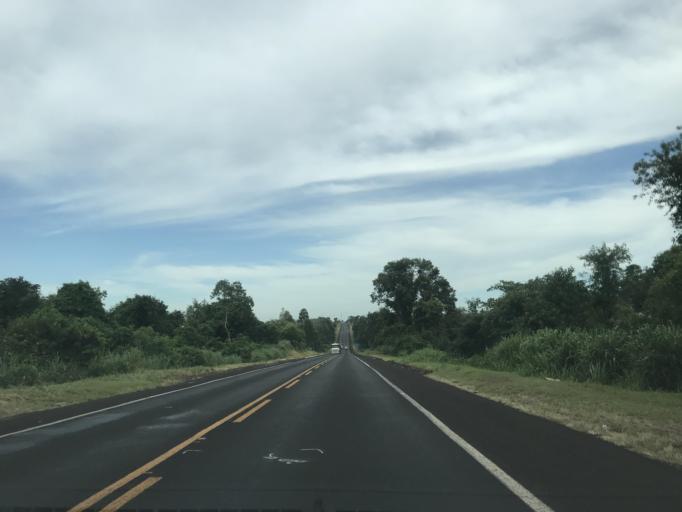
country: BR
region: Parana
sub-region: Paranavai
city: Paranavai
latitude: -23.0194
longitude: -52.5015
